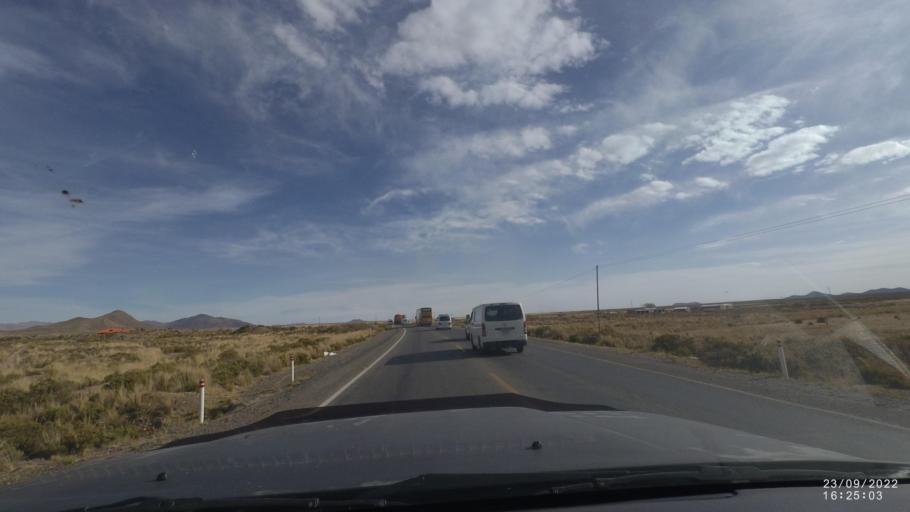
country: BO
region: Oruro
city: Machacamarca
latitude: -18.0876
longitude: -67.0100
